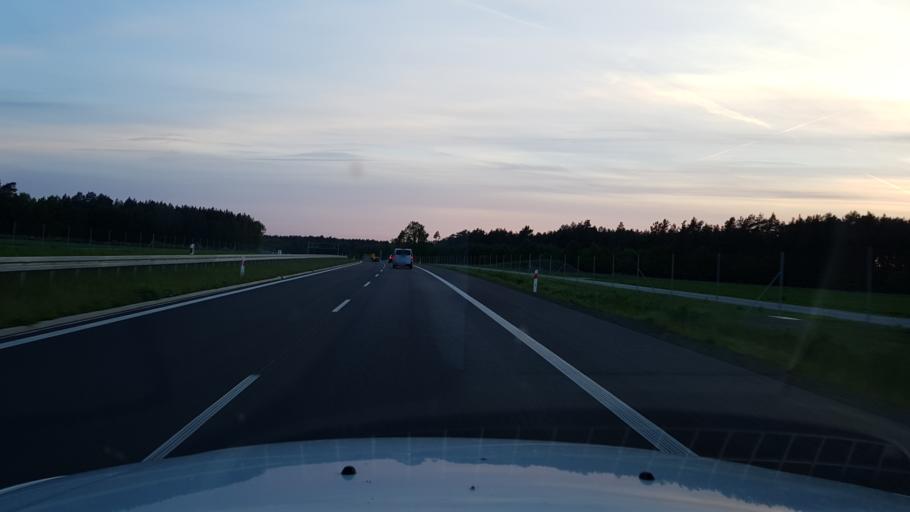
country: PL
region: West Pomeranian Voivodeship
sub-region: Powiat goleniowski
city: Osina
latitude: 53.6383
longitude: 15.0136
